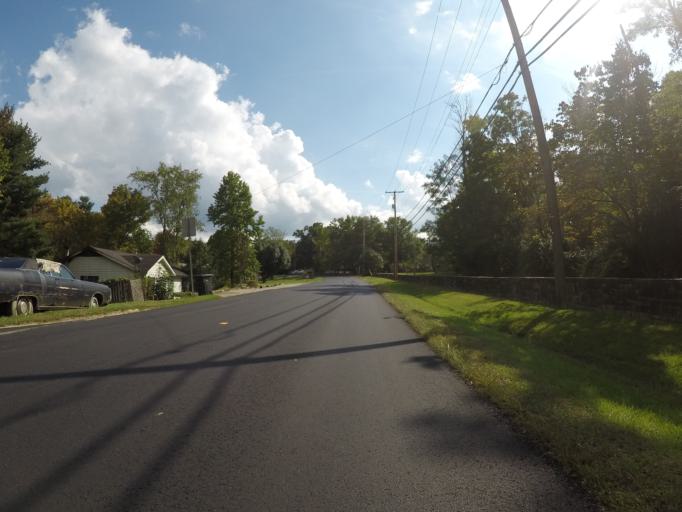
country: US
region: West Virginia
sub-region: Cabell County
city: Huntington
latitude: 38.3948
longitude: -82.4328
